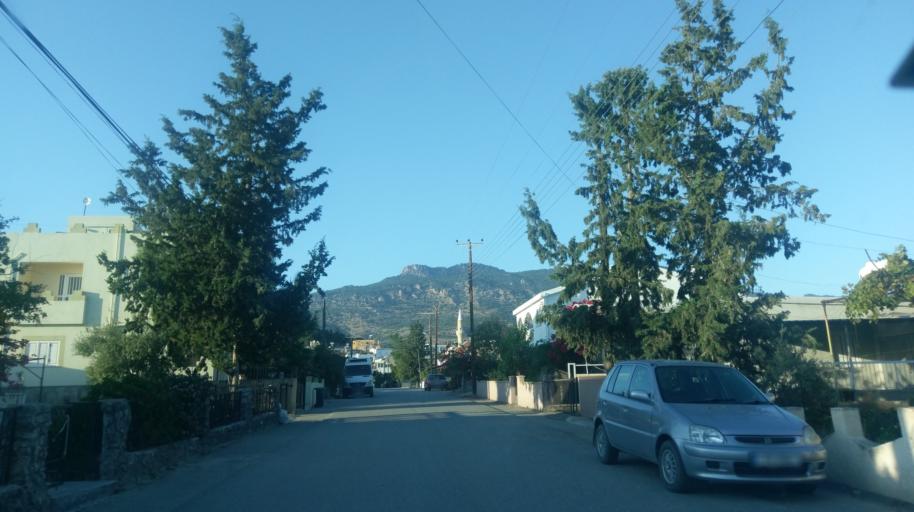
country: CY
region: Ammochostos
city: Lefkonoiko
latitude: 35.2555
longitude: 33.5495
